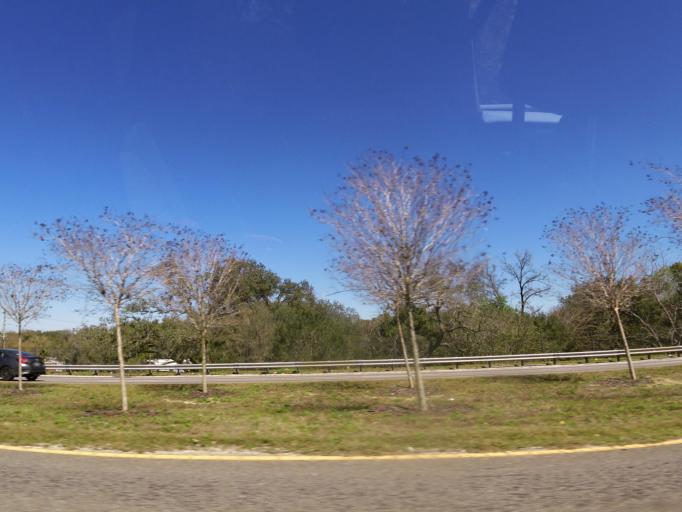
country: US
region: Florida
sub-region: Orange County
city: Lockhart
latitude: 28.6250
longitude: -81.4468
